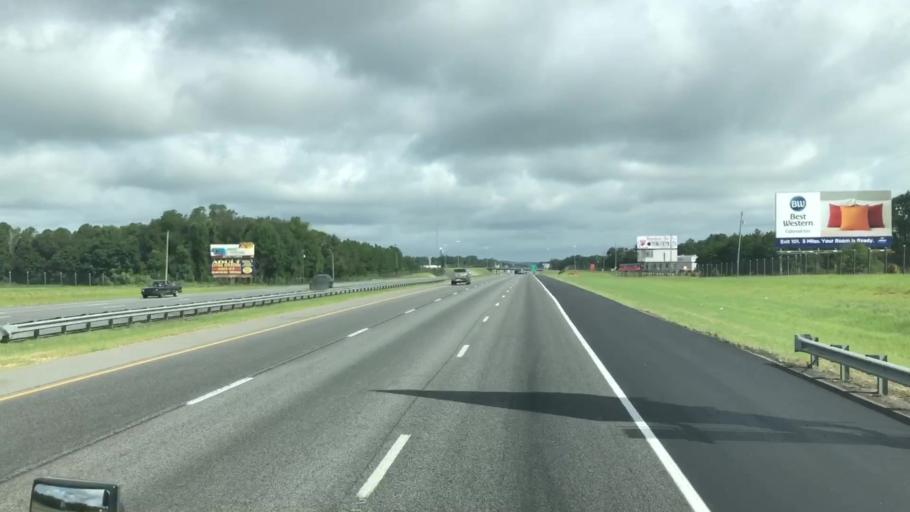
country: US
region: Georgia
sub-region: Crisp County
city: Cordele
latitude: 31.8987
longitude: -83.7341
